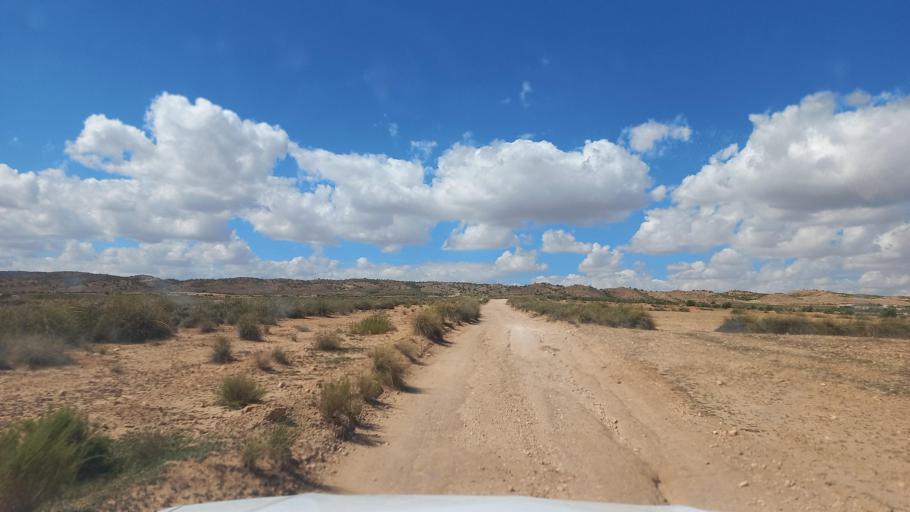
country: TN
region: Al Qasrayn
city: Sbiba
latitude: 35.3586
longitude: 9.0076
